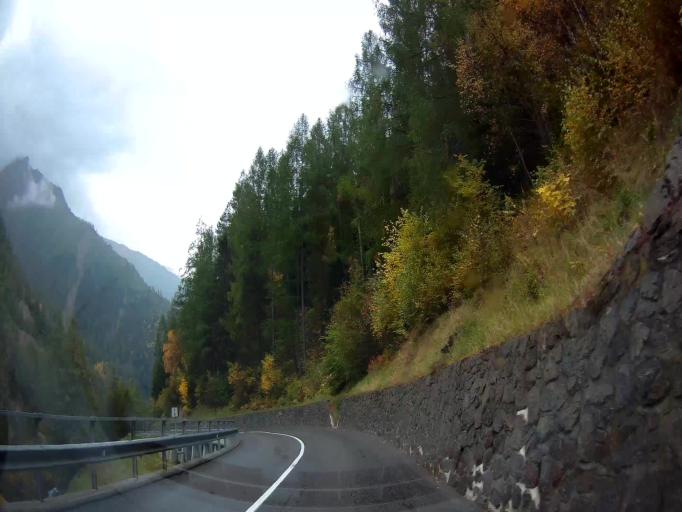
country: IT
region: Trentino-Alto Adige
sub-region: Bolzano
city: Senales
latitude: 46.7082
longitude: 10.9072
